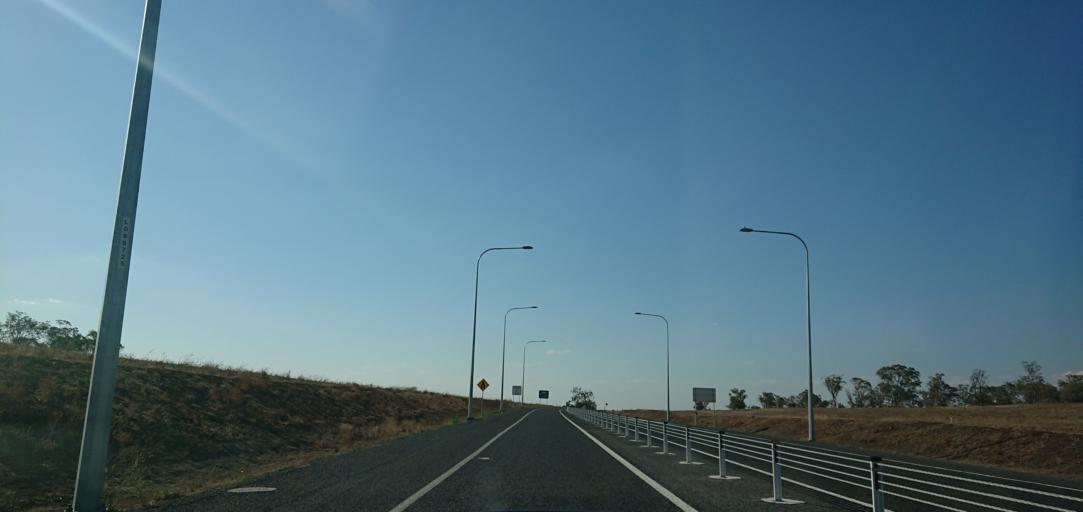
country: AU
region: Queensland
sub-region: Toowoomba
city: Westbrook
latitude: -27.6092
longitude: 151.7865
